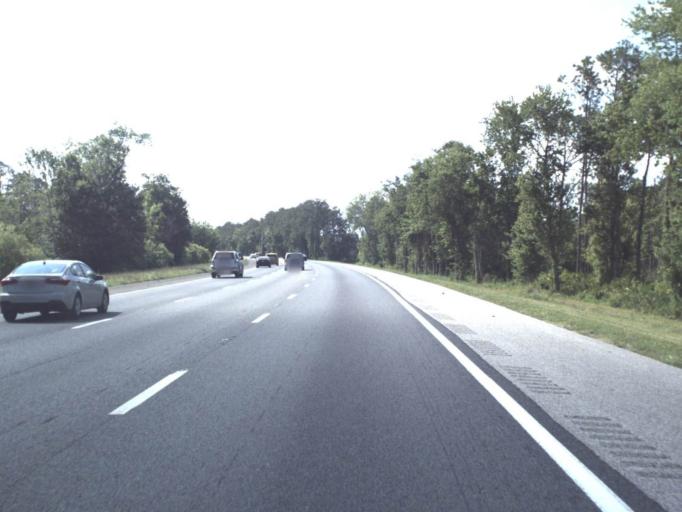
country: US
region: Florida
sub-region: Saint Johns County
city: Butler Beach
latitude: 29.6799
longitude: -81.3179
